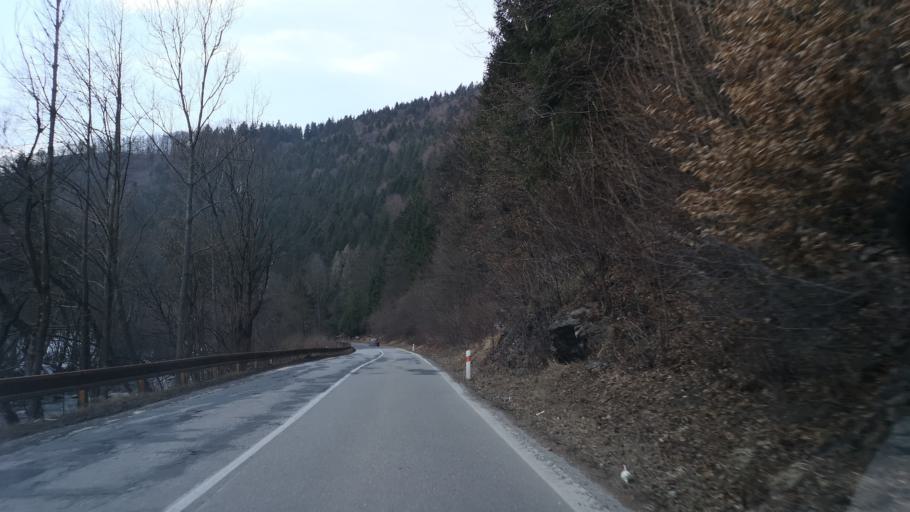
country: SK
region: Zilinsky
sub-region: Okres Dolny Kubin
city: Dolny Kubin
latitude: 49.2052
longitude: 19.1737
